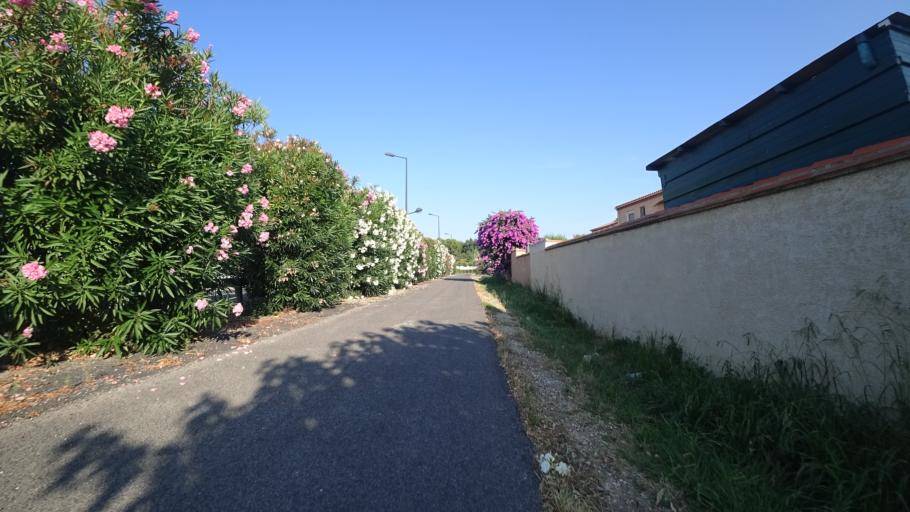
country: FR
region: Languedoc-Roussillon
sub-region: Departement des Pyrenees-Orientales
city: Bompas
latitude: 42.7223
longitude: 2.9278
